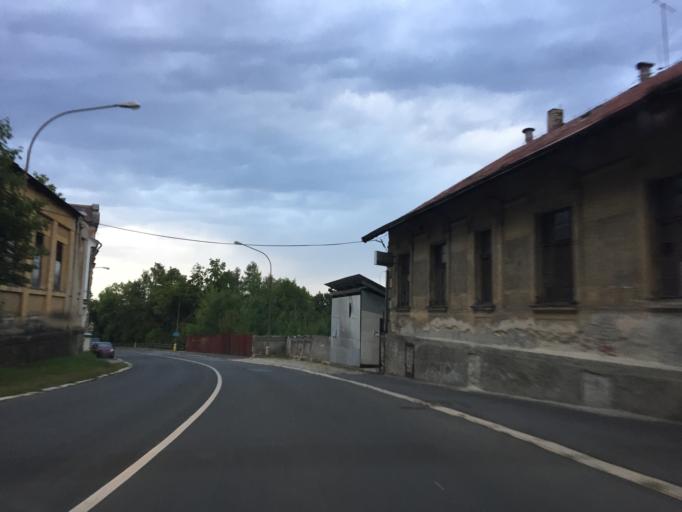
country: CZ
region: Liberecky
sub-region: Okres Jablonec nad Nisou
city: Jablonec nad Nisou
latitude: 50.7130
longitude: 15.1738
